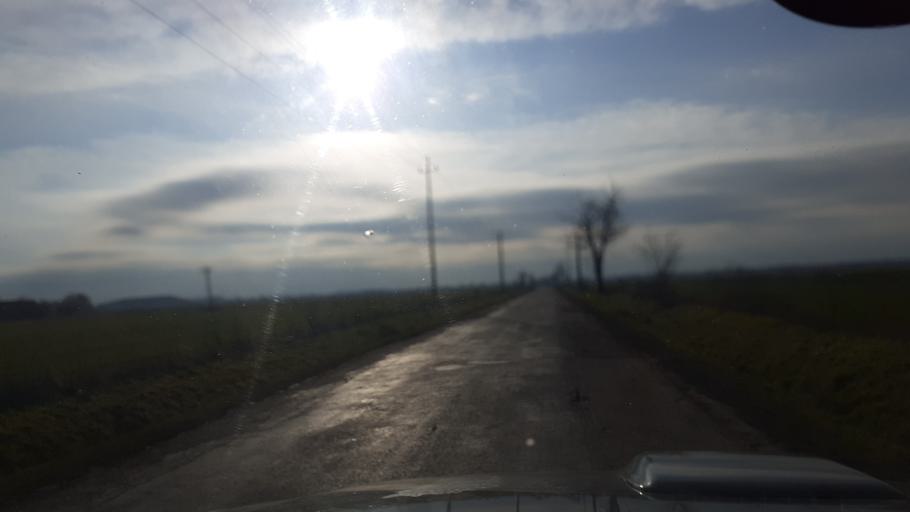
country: HU
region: Pest
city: Domsod
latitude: 47.1072
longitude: 19.0535
